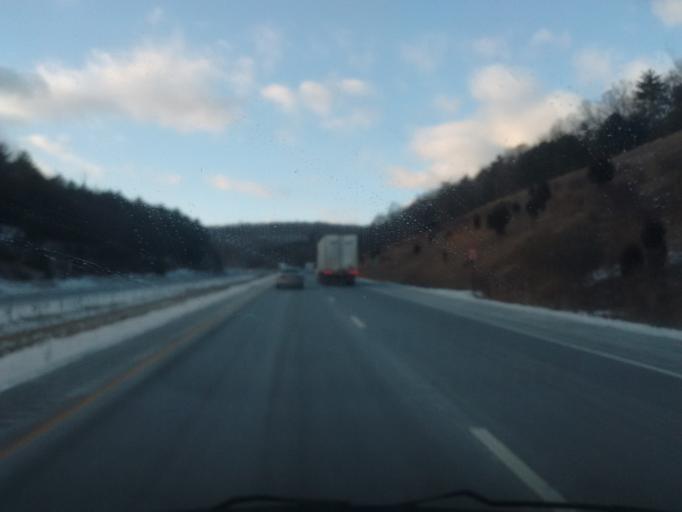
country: US
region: Pennsylvania
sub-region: Pike County
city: Milford
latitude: 41.3432
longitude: -74.7832
